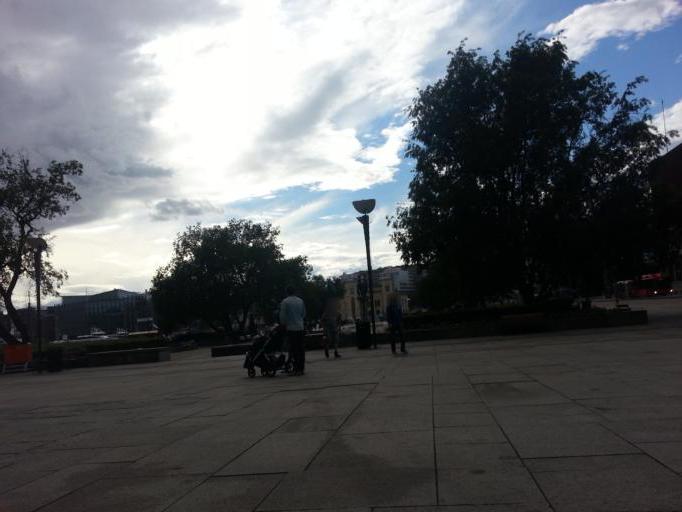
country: NO
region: Oslo
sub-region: Oslo
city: Oslo
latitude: 59.9109
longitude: 10.7347
